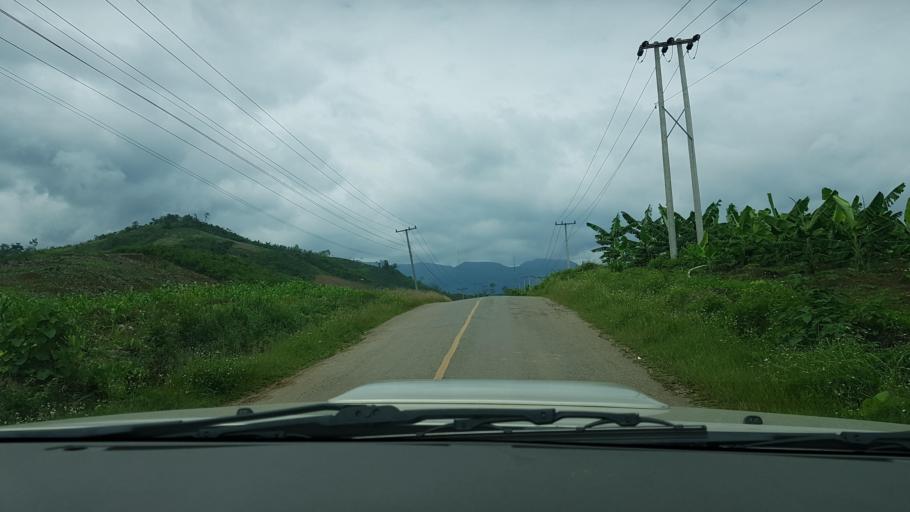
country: TH
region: Nan
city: Chaloem Phra Kiat
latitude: 19.9820
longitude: 101.2742
